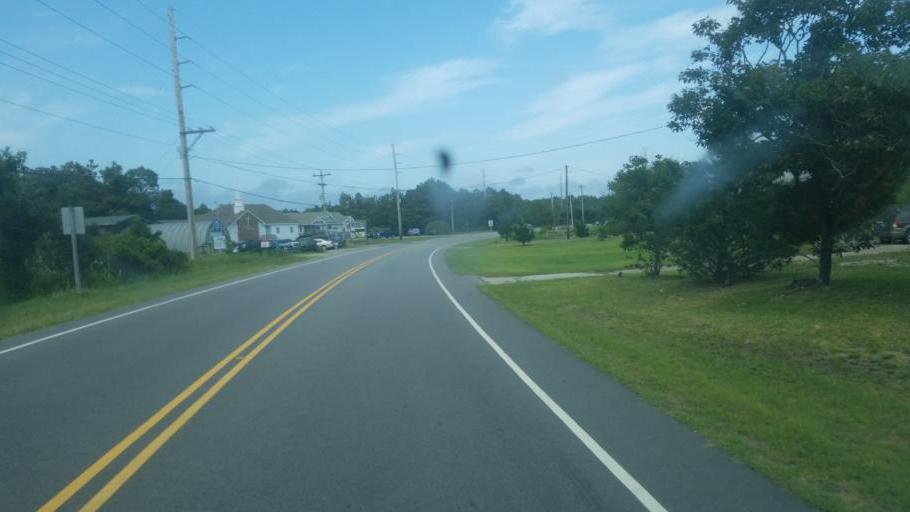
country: US
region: North Carolina
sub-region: Dare County
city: Buxton
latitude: 35.2585
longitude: -75.5884
